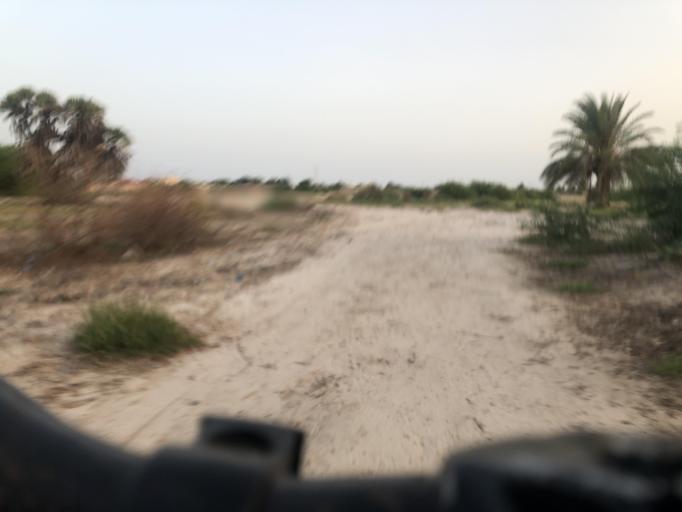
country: SN
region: Saint-Louis
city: Saint-Louis
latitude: 16.0731
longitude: -16.4319
